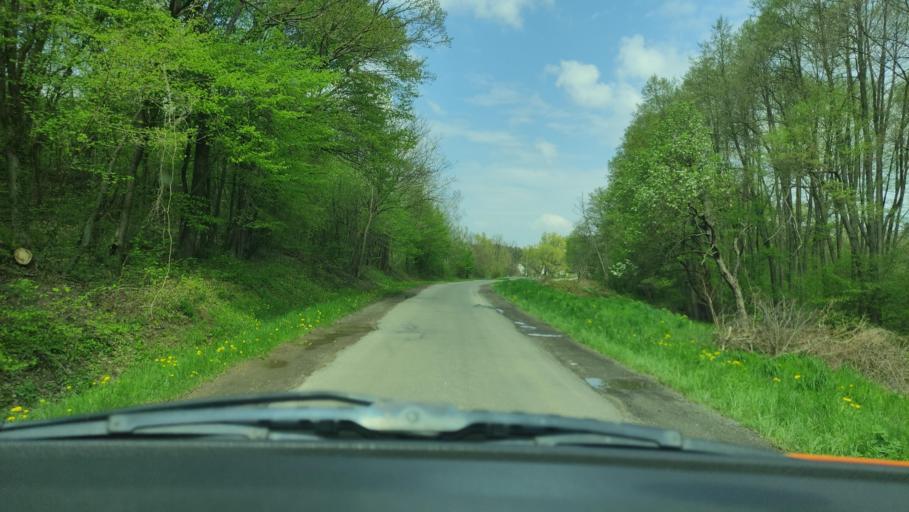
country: HU
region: Baranya
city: Sasd
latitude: 46.2842
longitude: 18.1032
